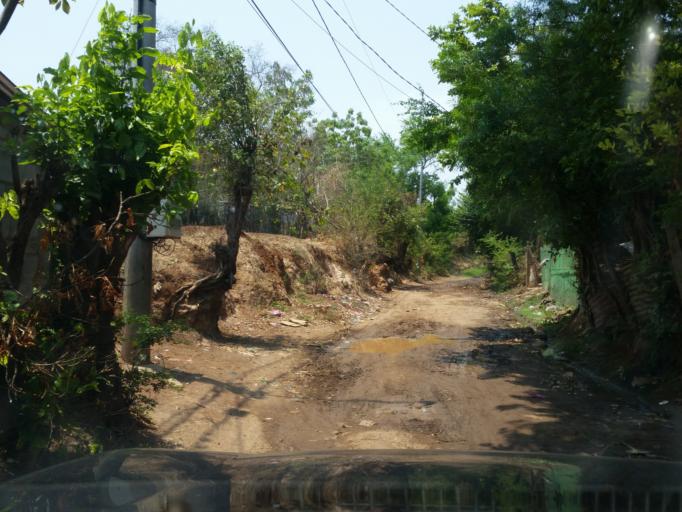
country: NI
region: Granada
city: Granada
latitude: 11.9182
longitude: -85.9605
